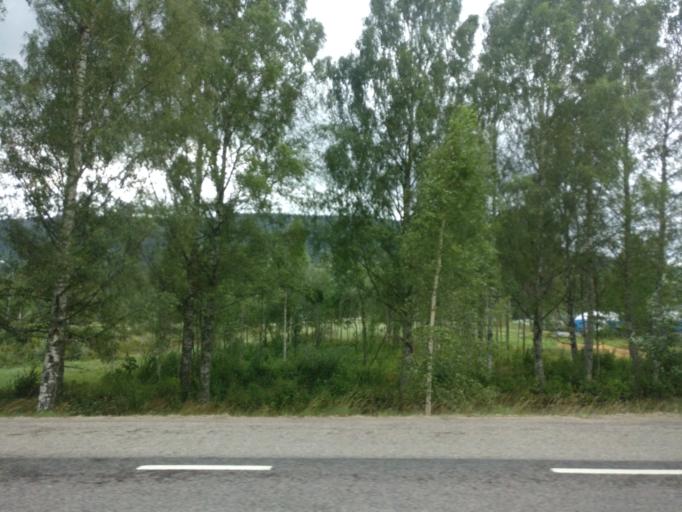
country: SE
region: Vaermland
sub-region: Torsby Kommun
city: Torsby
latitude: 60.7318
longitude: 12.8698
